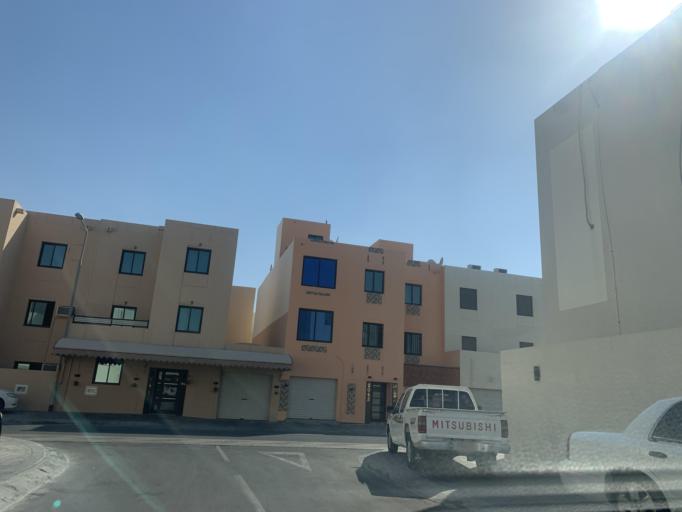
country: BH
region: Central Governorate
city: Madinat Hamad
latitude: 26.1225
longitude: 50.4845
